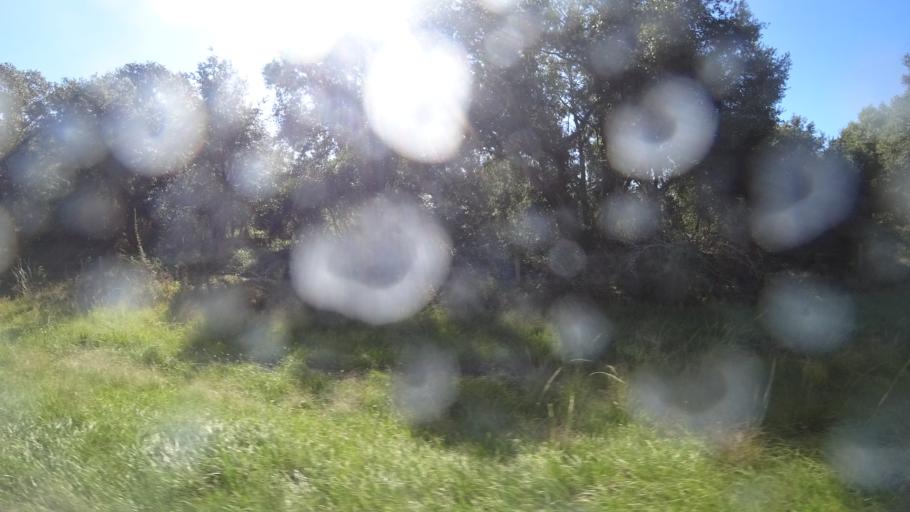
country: US
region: Florida
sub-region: Hillsborough County
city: Wimauma
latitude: 27.6642
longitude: -82.3039
